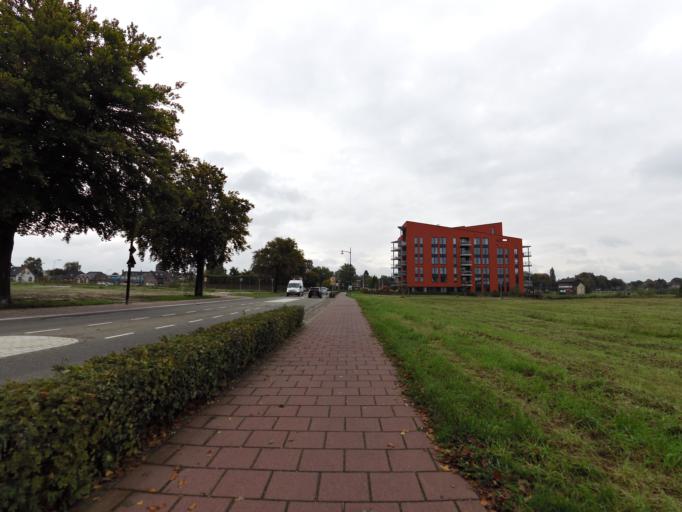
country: NL
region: Gelderland
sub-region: Oude IJsselstreek
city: Gendringen
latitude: 51.8885
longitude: 6.3859
